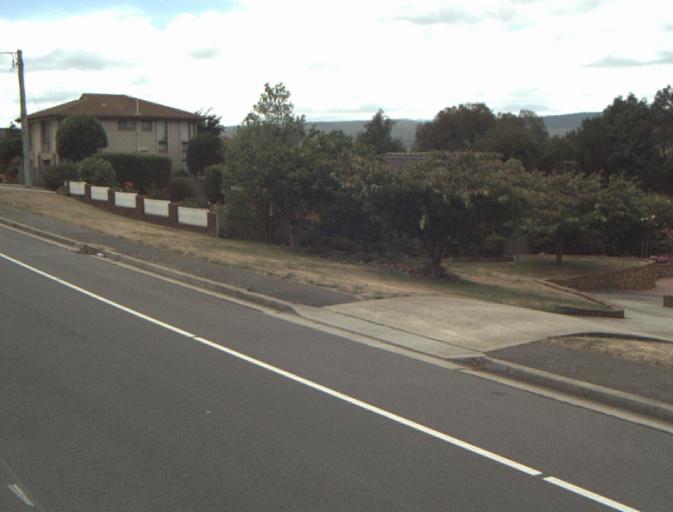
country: AU
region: Tasmania
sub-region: Launceston
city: Newstead
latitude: -41.4605
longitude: 147.1822
